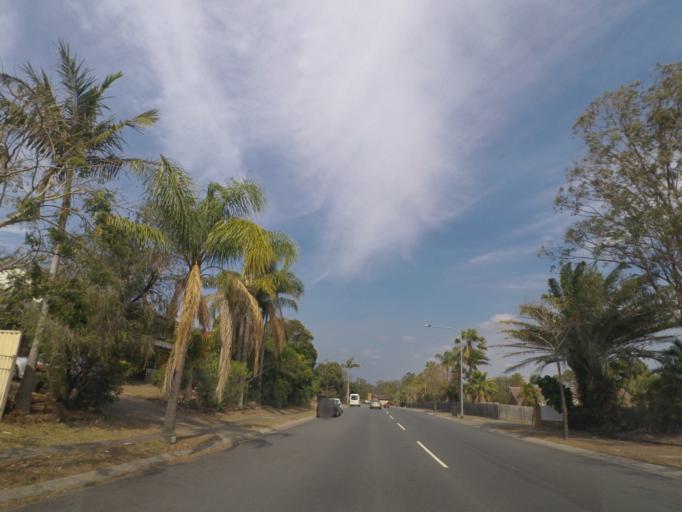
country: AU
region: Queensland
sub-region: Brisbane
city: Sunnybank Hills
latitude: -27.6000
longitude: 153.0622
